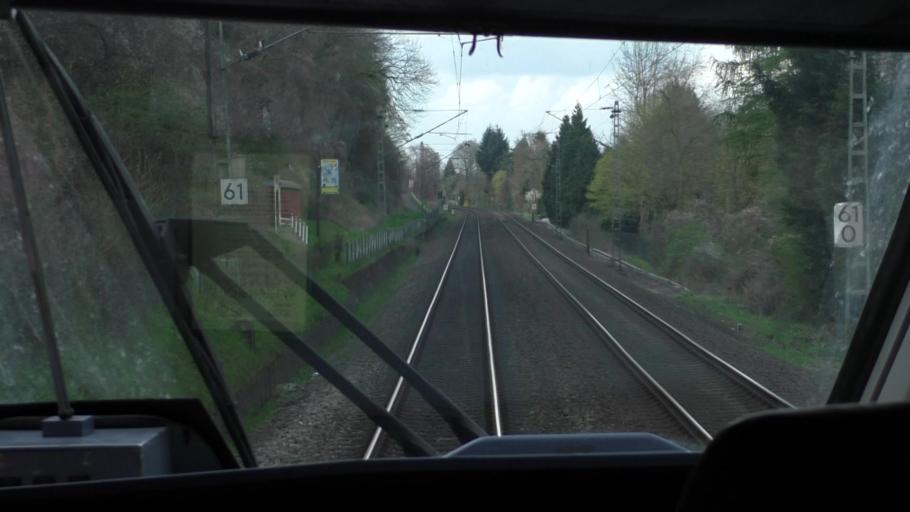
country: DE
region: Rheinland-Pfalz
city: Bad Breisig
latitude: 50.5140
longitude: 7.2917
